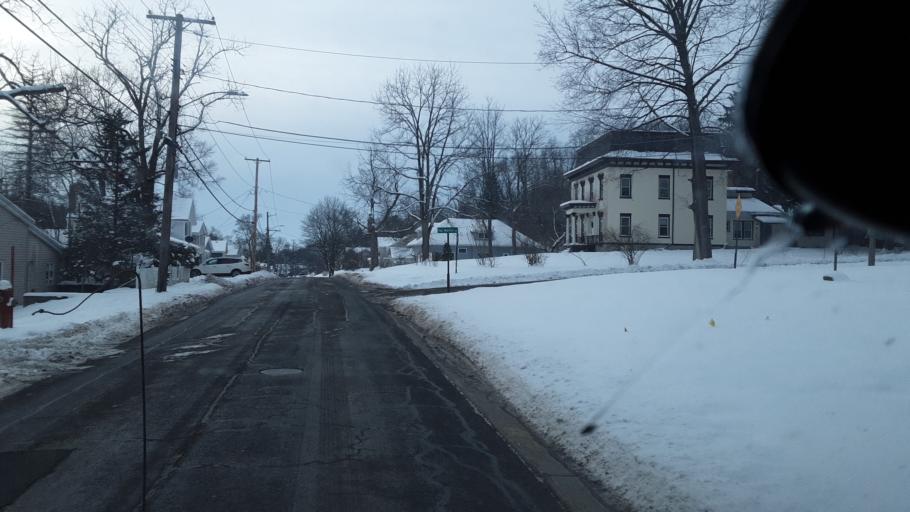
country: US
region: New York
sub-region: Wayne County
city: Lyons
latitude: 43.0746
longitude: -76.9939
